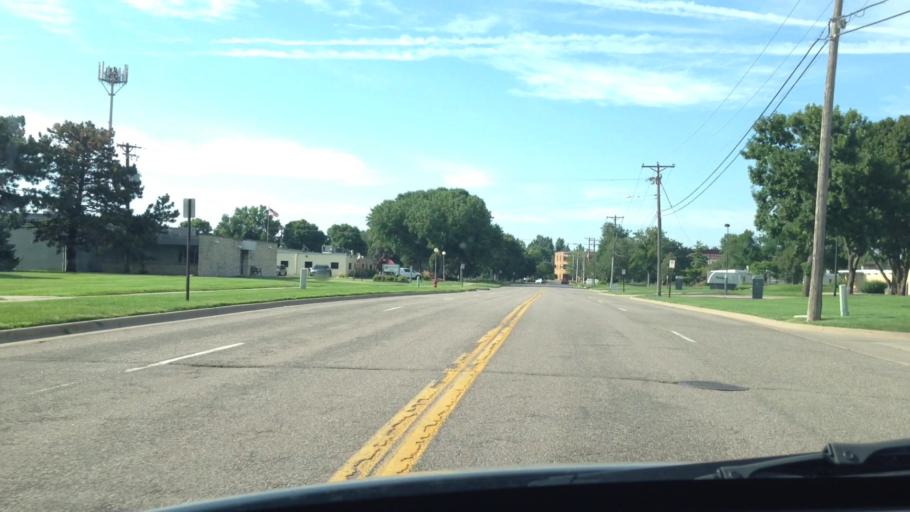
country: US
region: Minnesota
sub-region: Hennepin County
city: Edina
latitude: 44.8600
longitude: -93.3457
